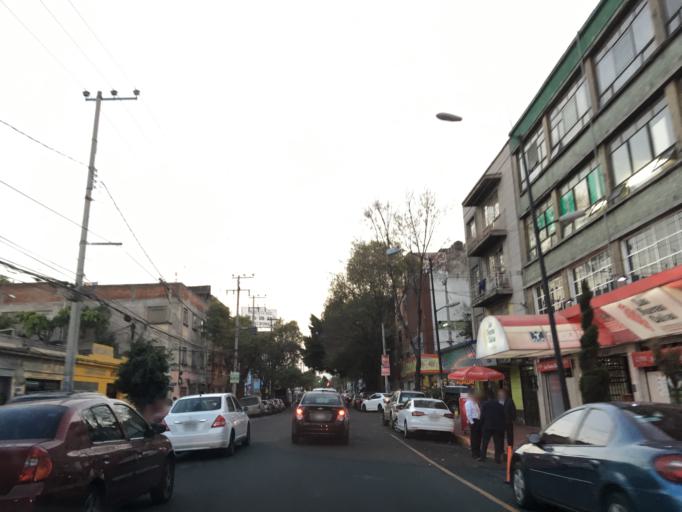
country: MX
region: Mexico City
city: Mexico City
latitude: 19.4184
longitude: -99.1407
